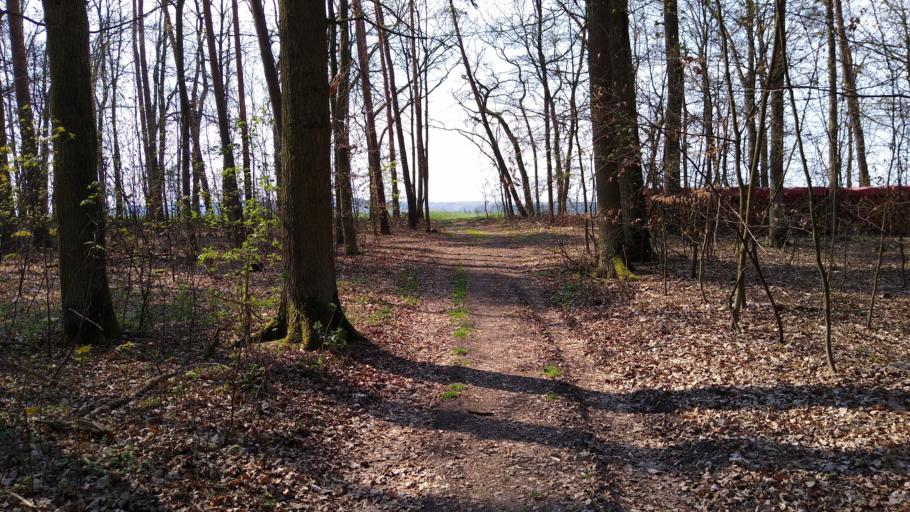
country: DE
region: Bavaria
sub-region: Regierungsbezirk Mittelfranken
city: Obermichelbach
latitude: 49.5027
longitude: 10.9171
